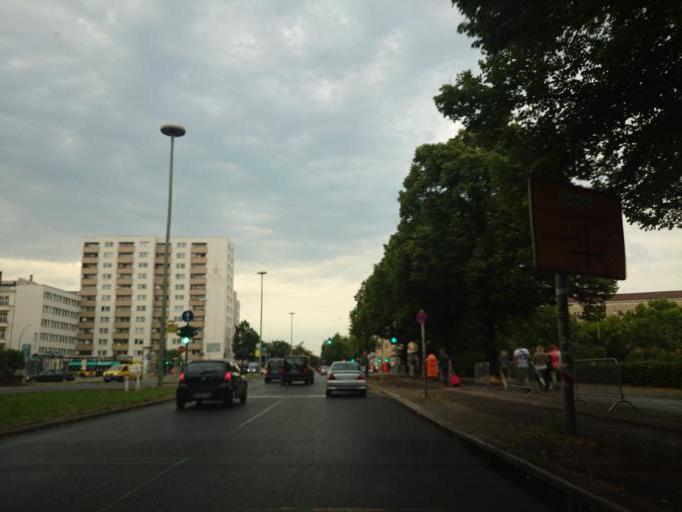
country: DE
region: Berlin
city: Tempelhof Bezirk
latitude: 52.4835
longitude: 13.3861
